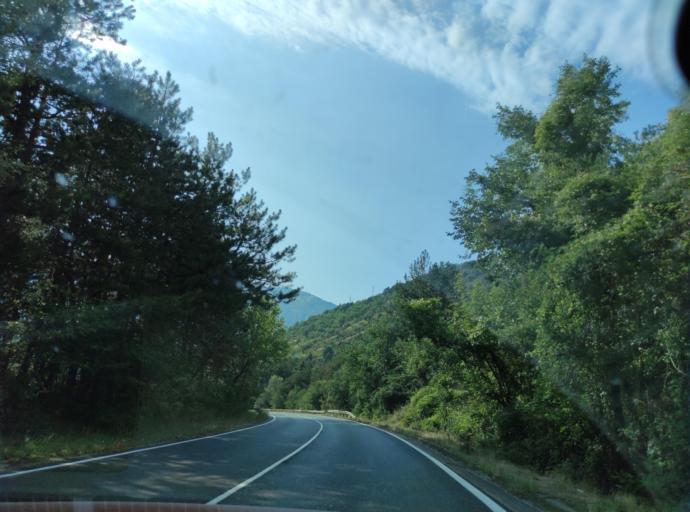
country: BG
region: Blagoevgrad
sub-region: Obshtina Kresna
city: Kresna
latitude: 41.7473
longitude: 23.1630
